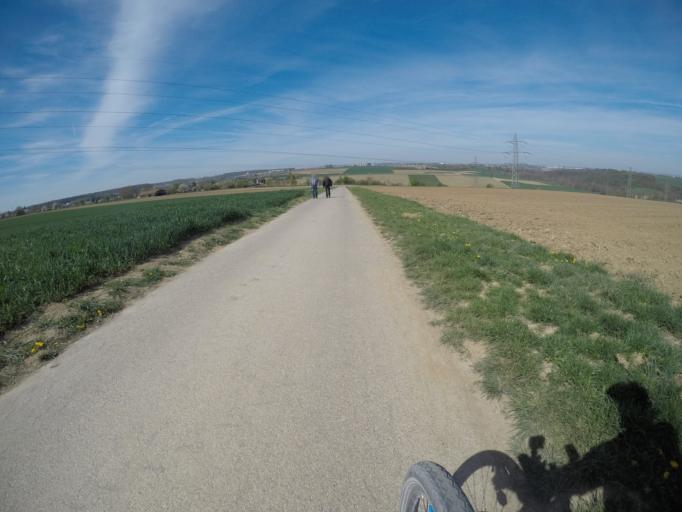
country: DE
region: Baden-Wuerttemberg
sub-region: Regierungsbezirk Stuttgart
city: Hemmingen
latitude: 48.8434
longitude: 9.0409
